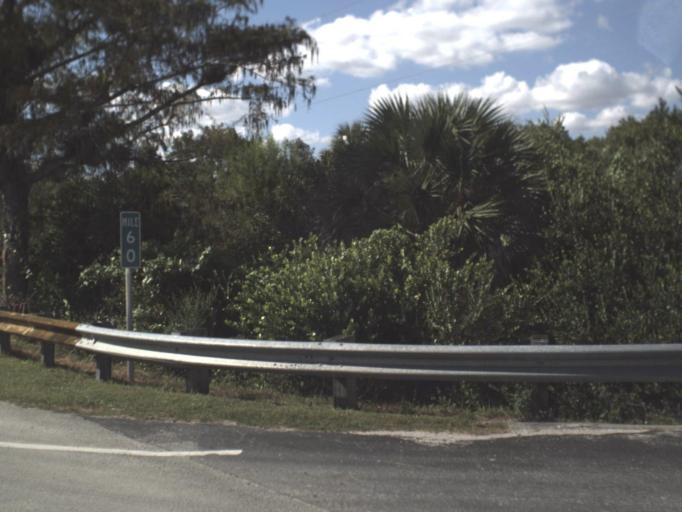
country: US
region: Florida
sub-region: Collier County
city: Lely Resort
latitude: 25.8651
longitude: -81.1140
